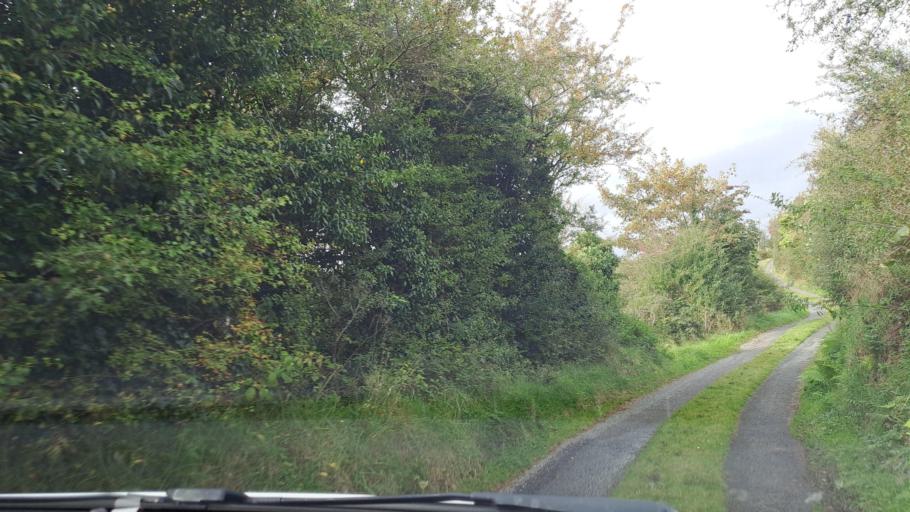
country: IE
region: Ulster
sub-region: An Cabhan
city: Bailieborough
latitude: 54.0012
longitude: -6.9415
